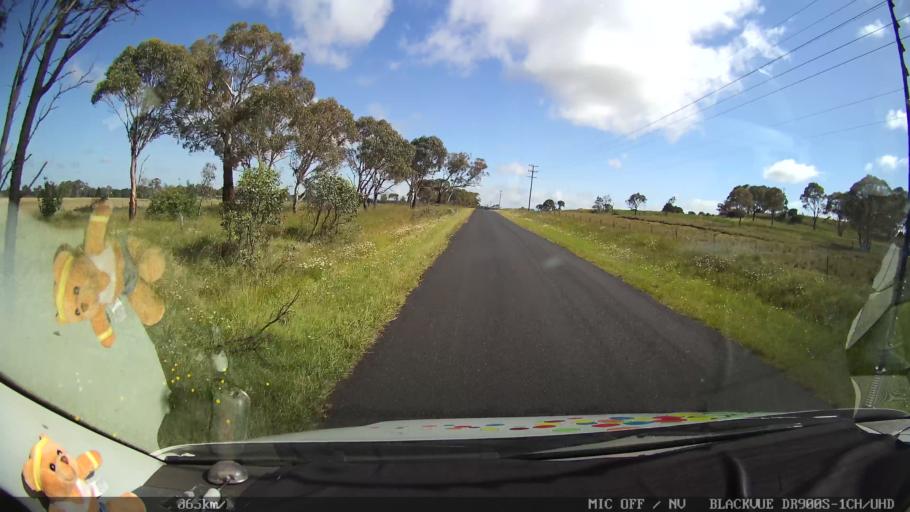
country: AU
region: New South Wales
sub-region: Guyra
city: Guyra
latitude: -30.1978
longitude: 151.6756
